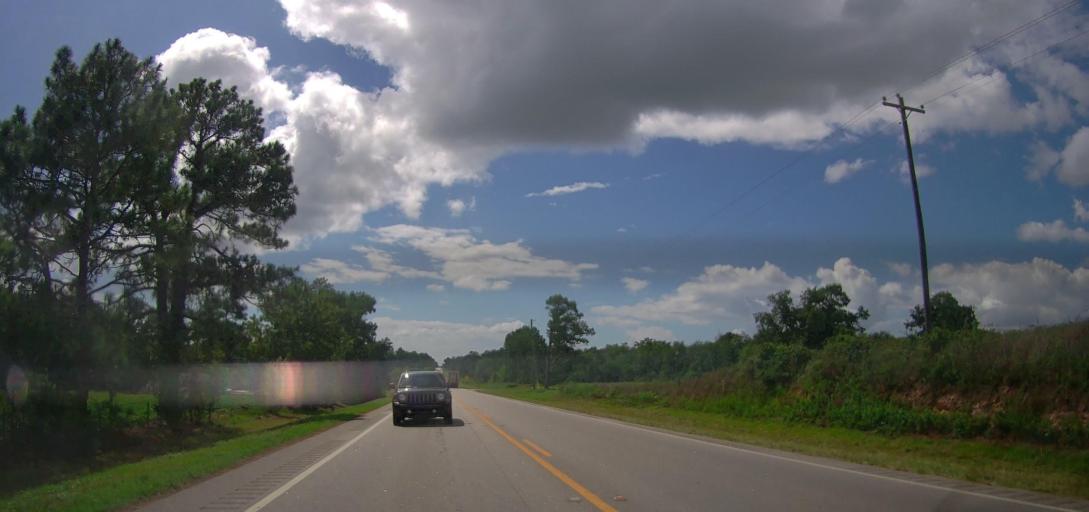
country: US
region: Georgia
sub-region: Coffee County
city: Broxton
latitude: 31.5617
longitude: -82.9873
